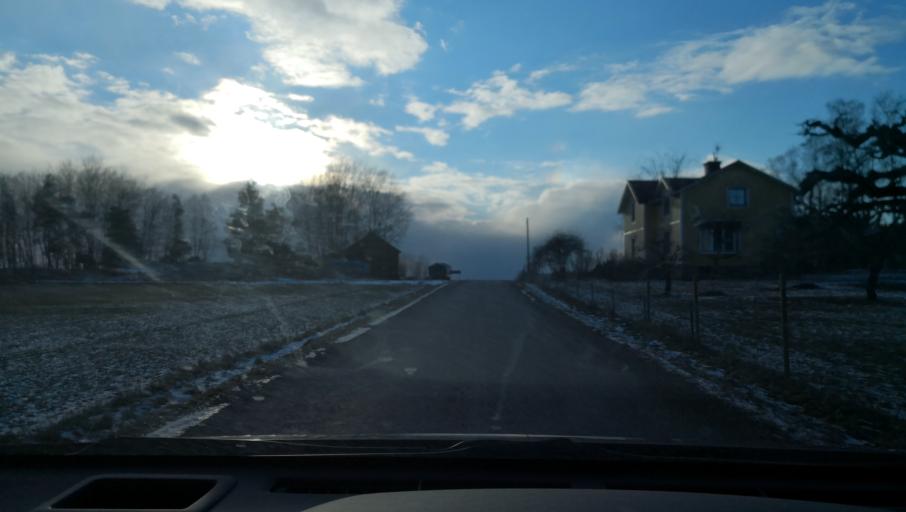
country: SE
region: Uppsala
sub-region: Enkopings Kommun
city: Irsta
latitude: 59.6610
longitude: 16.8235
